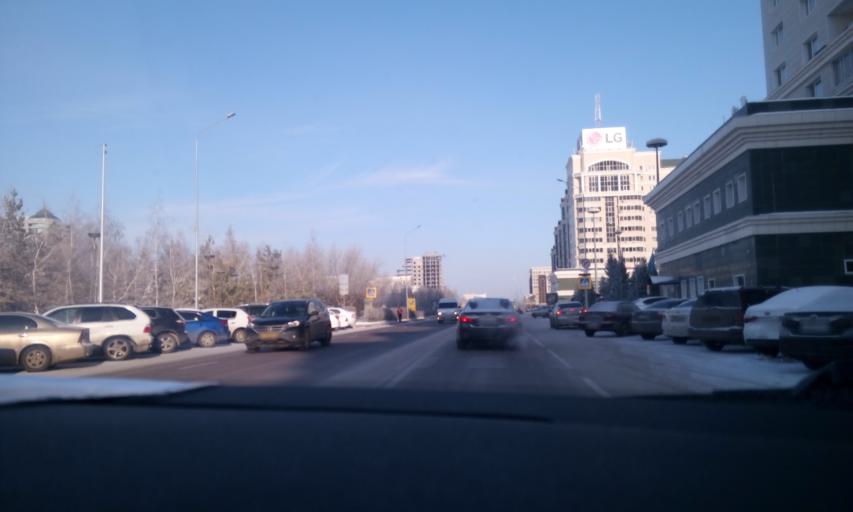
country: KZ
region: Astana Qalasy
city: Astana
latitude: 51.1267
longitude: 71.4319
